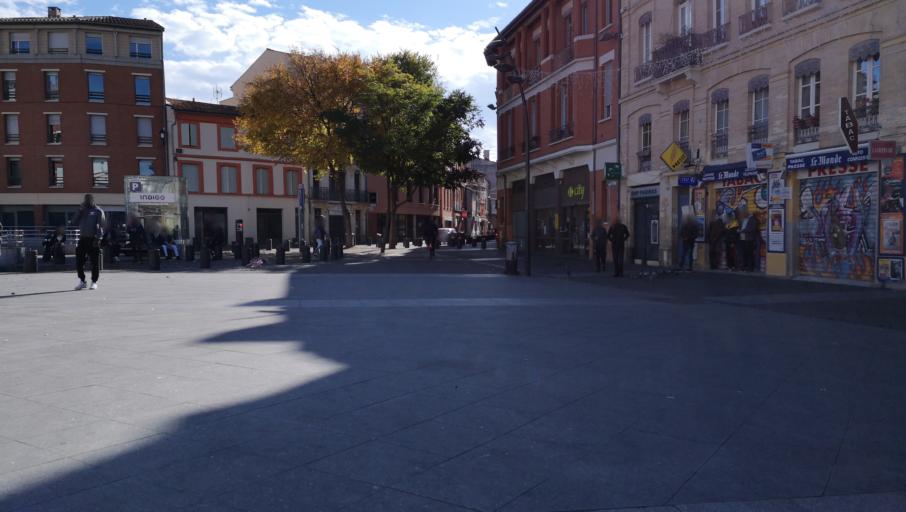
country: FR
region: Midi-Pyrenees
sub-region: Departement de la Haute-Garonne
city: Toulouse
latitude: 43.6108
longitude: 1.4390
